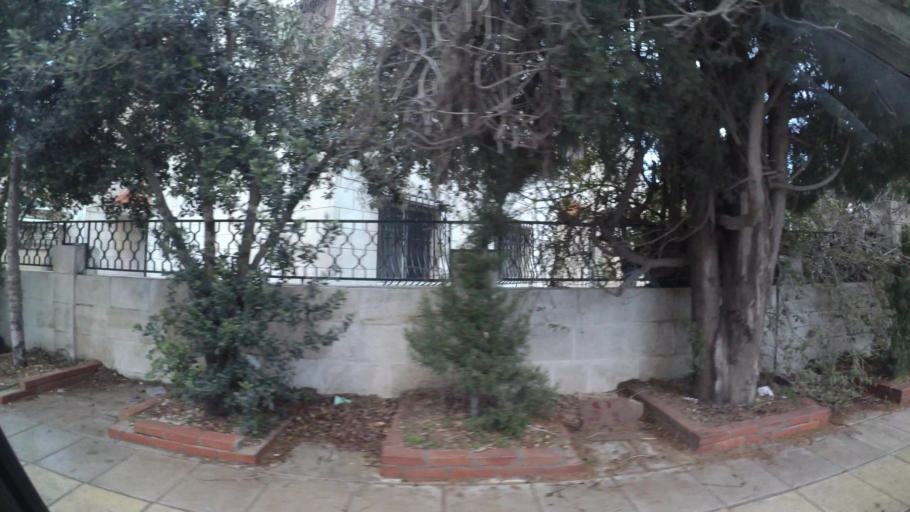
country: JO
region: Amman
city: Al Jubayhah
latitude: 32.0302
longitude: 35.8252
